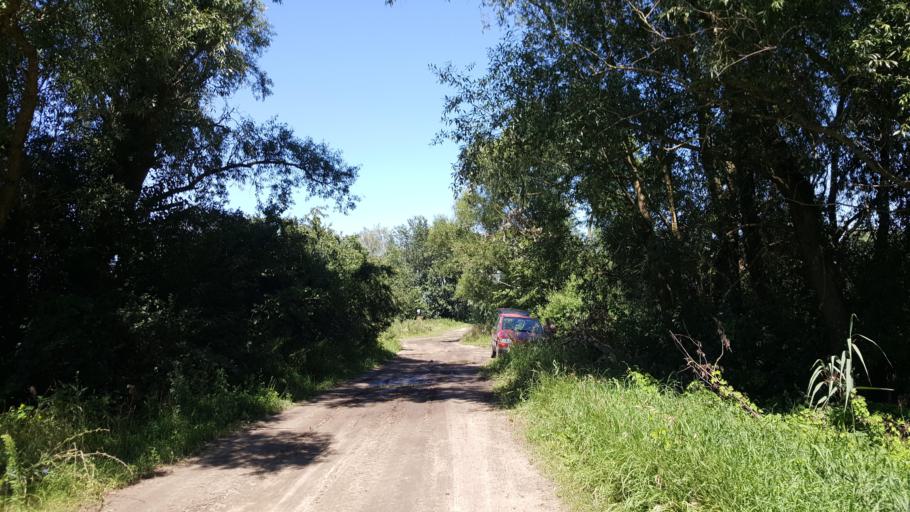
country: BY
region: Brest
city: Charnawchytsy
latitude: 52.2280
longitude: 23.7826
